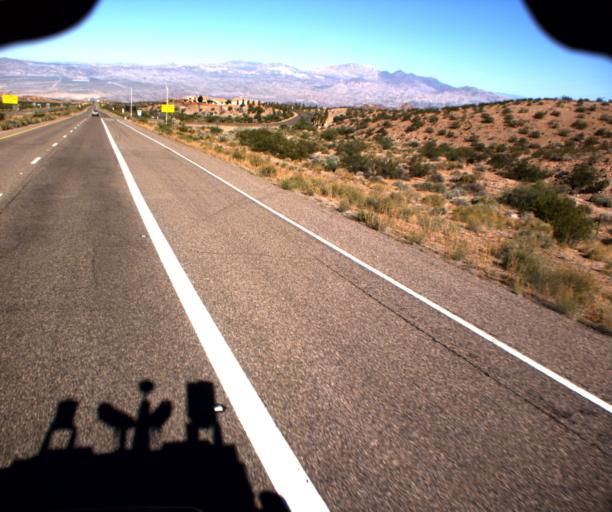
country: US
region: Nevada
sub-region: Clark County
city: Laughlin
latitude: 35.1857
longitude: -114.4564
